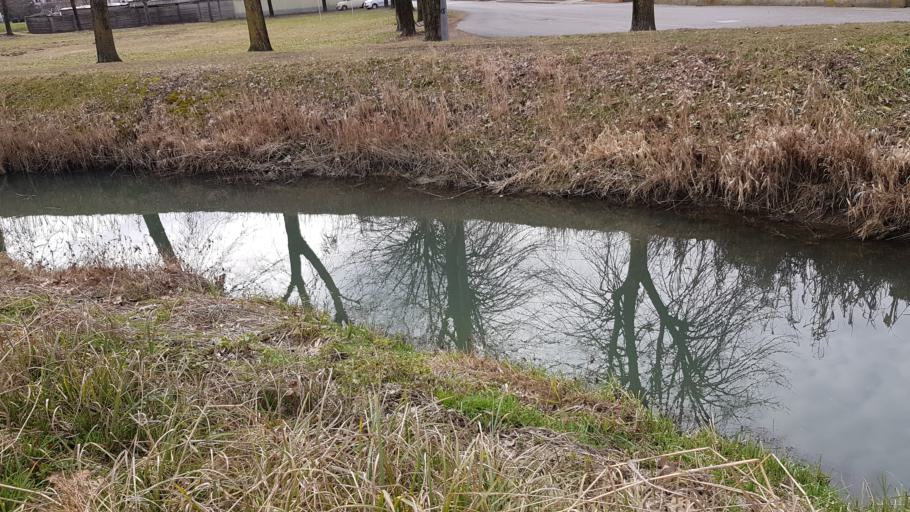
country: IT
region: Veneto
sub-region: Provincia di Padova
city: San Giorgio delle Pertiche
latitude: 45.5442
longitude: 11.9095
